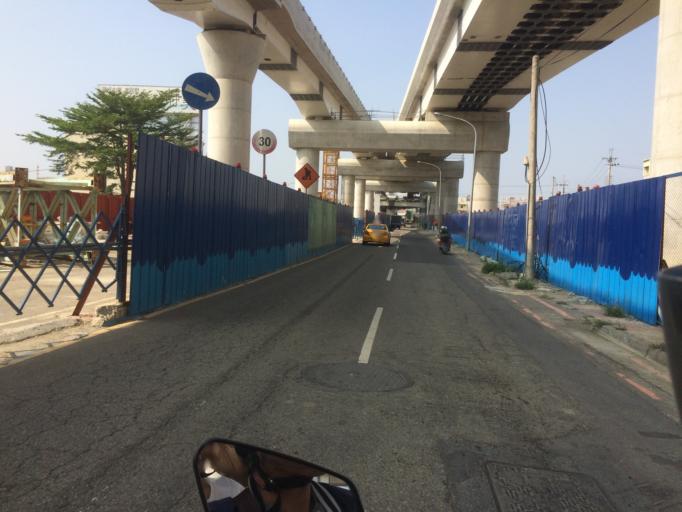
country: TW
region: Taiwan
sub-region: Taichung City
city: Taichung
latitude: 24.1824
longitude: 120.7096
